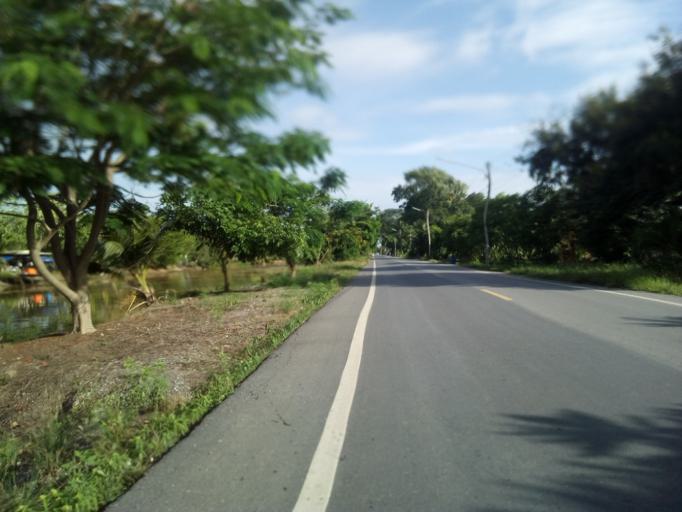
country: TH
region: Pathum Thani
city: Nong Suea
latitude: 14.1079
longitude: 100.8461
